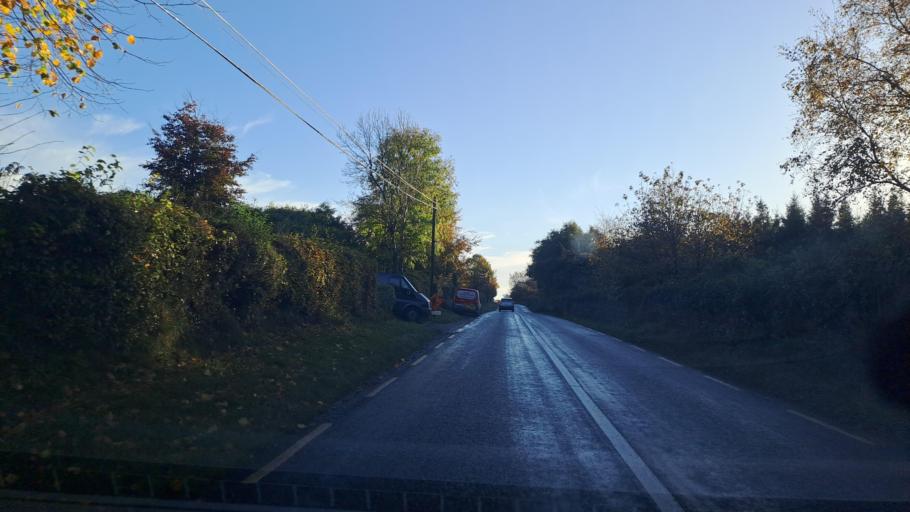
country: IE
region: Ulster
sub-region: An Cabhan
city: Cootehill
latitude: 54.1138
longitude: -7.0360
